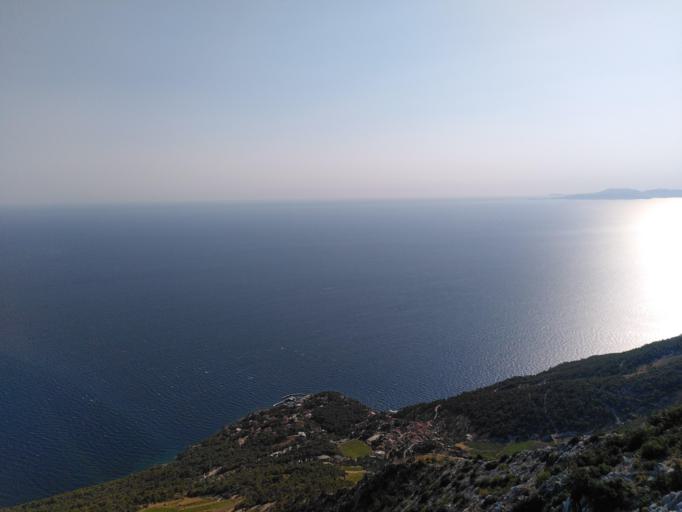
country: HR
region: Splitsko-Dalmatinska
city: Stari Grad
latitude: 43.1445
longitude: 16.5976
